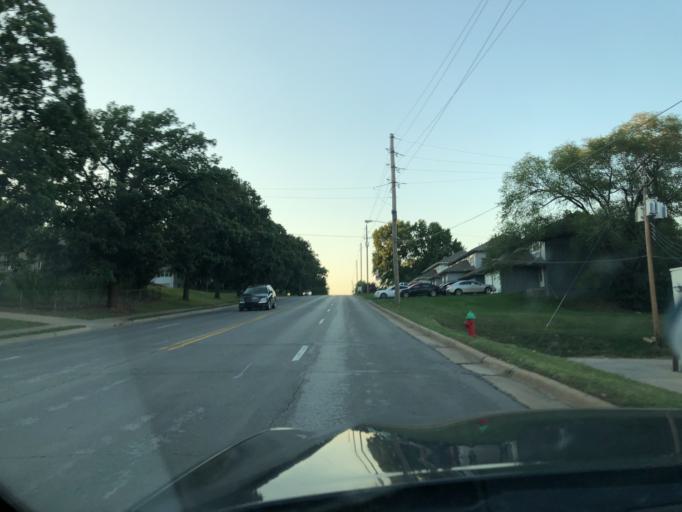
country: US
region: Kansas
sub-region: Leavenworth County
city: Leavenworth
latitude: 39.3116
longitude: -94.9507
